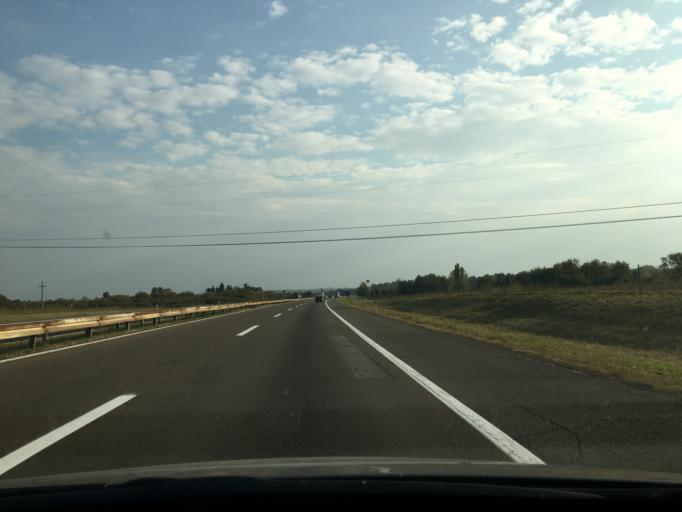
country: RS
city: Lugavcina
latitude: 44.5583
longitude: 20.9834
